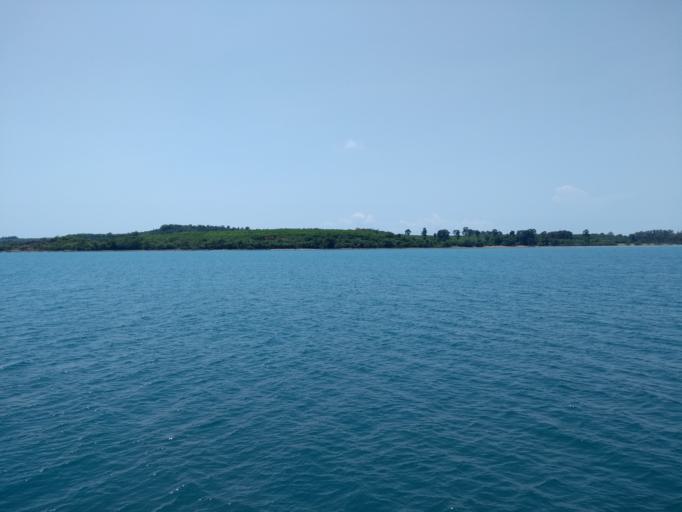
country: TH
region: Trat
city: Ko Kut
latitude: 11.8095
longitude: 102.5122
